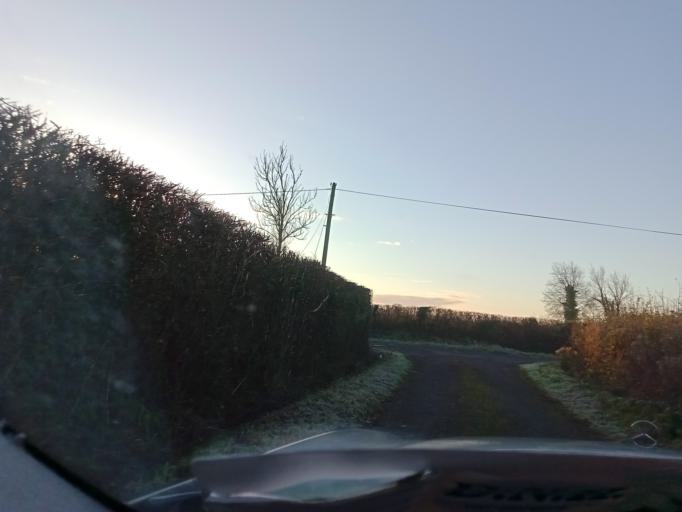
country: IE
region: Leinster
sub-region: Kilkenny
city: Callan
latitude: 52.5397
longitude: -7.4239
